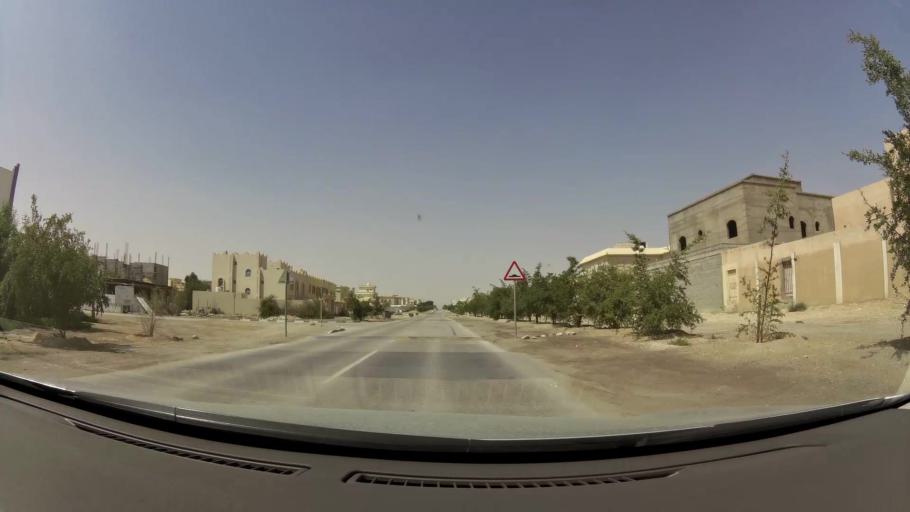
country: QA
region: Baladiyat Umm Salal
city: Umm Salal Muhammad
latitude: 25.3763
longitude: 51.4205
